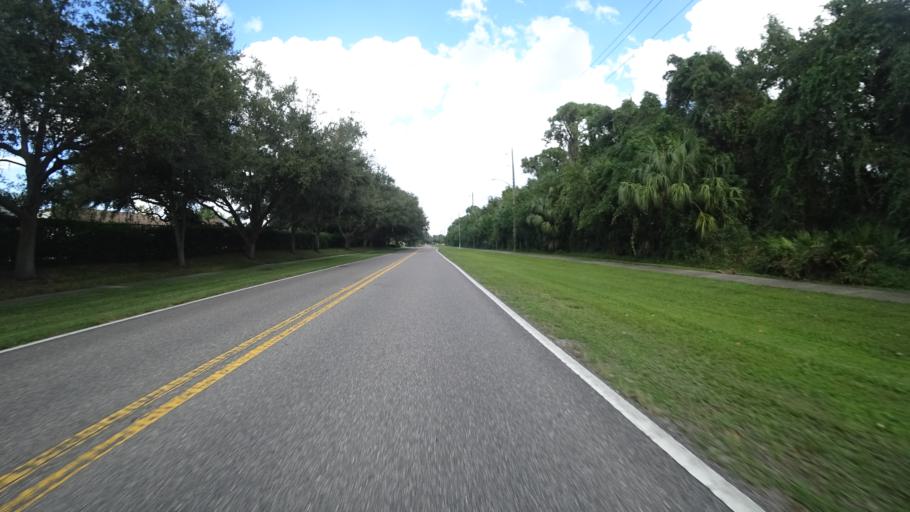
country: US
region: Florida
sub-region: Manatee County
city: Samoset
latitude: 27.4339
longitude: -82.5136
